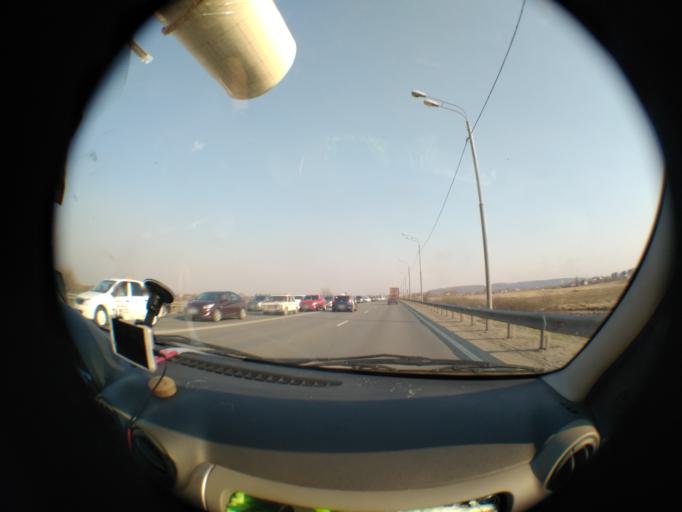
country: RU
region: Moskovskaya
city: Ostrovtsy
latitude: 55.5798
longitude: 38.0183
